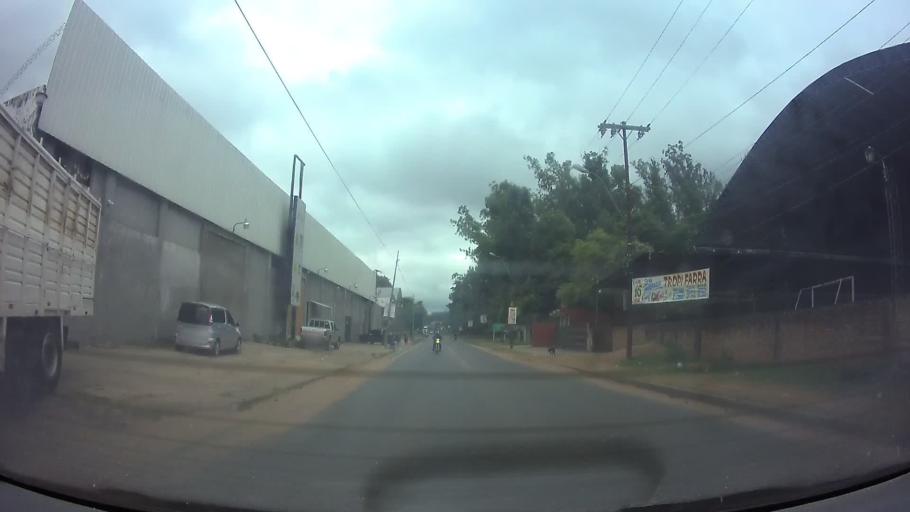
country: PY
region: Central
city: Nemby
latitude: -25.3835
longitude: -57.5476
